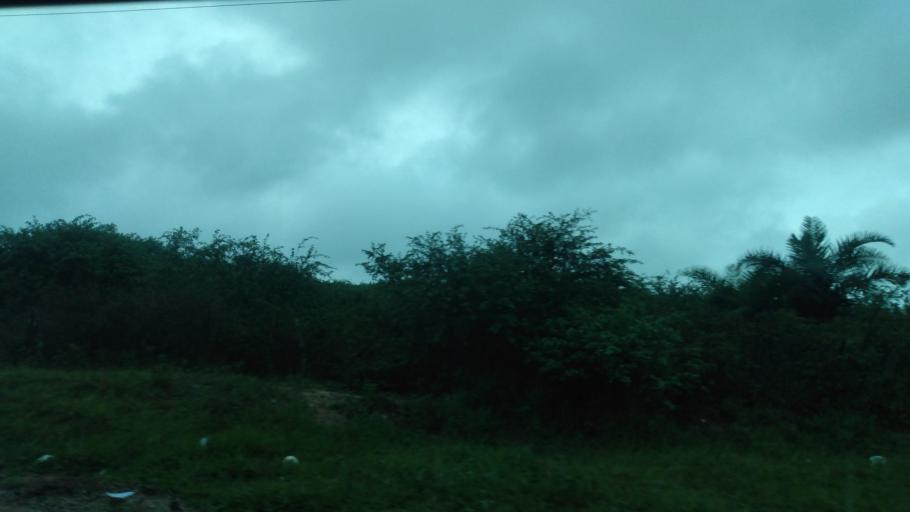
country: BR
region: Pernambuco
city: Garanhuns
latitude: -8.8509
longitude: -36.5154
